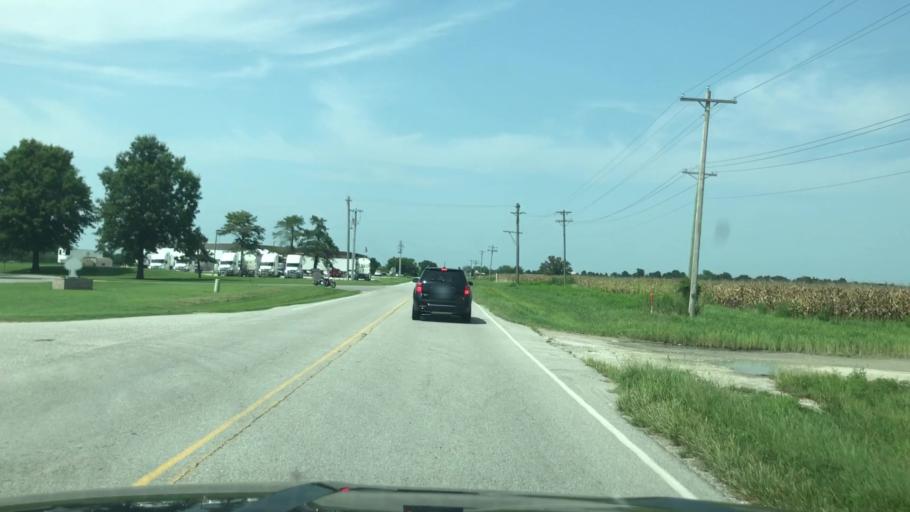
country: US
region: Oklahoma
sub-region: Ottawa County
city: Commerce
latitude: 36.9135
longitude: -94.8419
